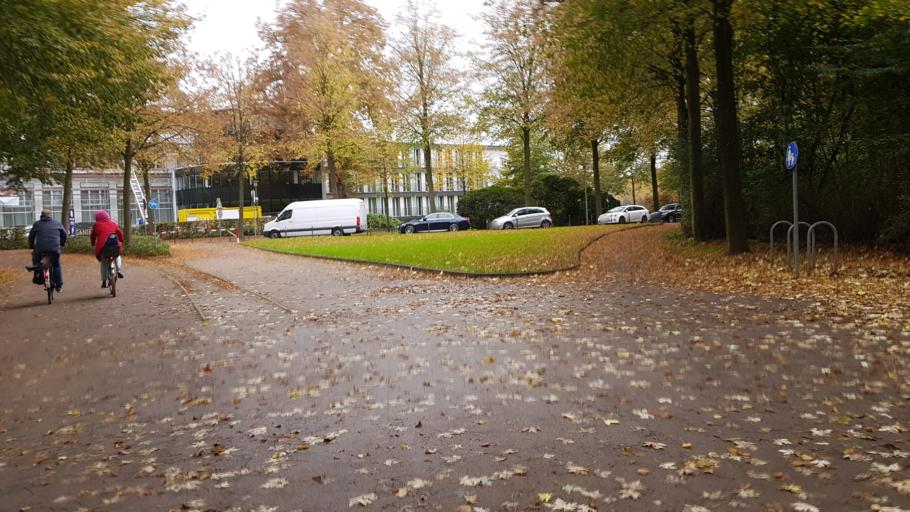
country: DE
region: Bremen
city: Bremen
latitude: 53.0900
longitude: 8.8202
